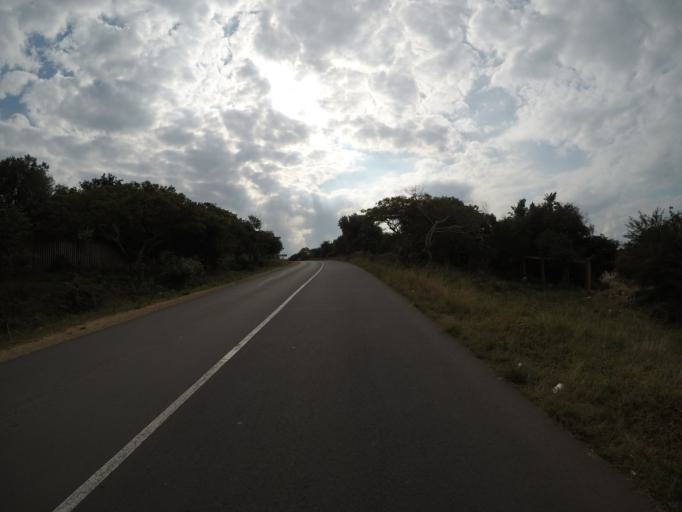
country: ZA
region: KwaZulu-Natal
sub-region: uThungulu District Municipality
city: Richards Bay
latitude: -28.7464
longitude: 32.0850
